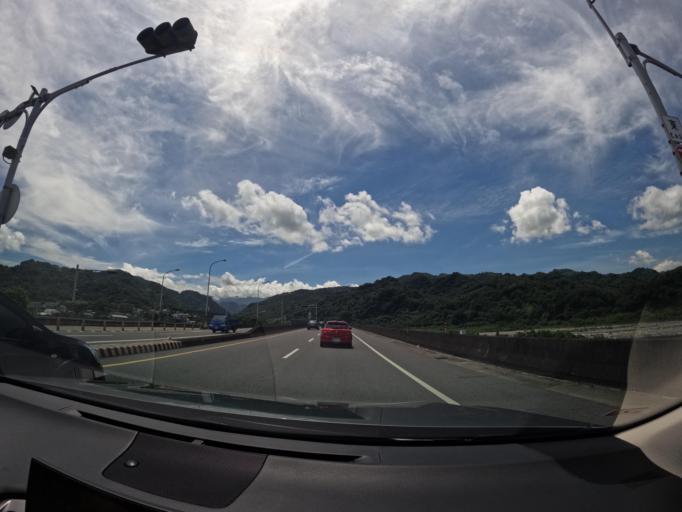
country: TW
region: Taiwan
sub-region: Miaoli
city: Miaoli
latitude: 24.4663
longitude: 120.8233
